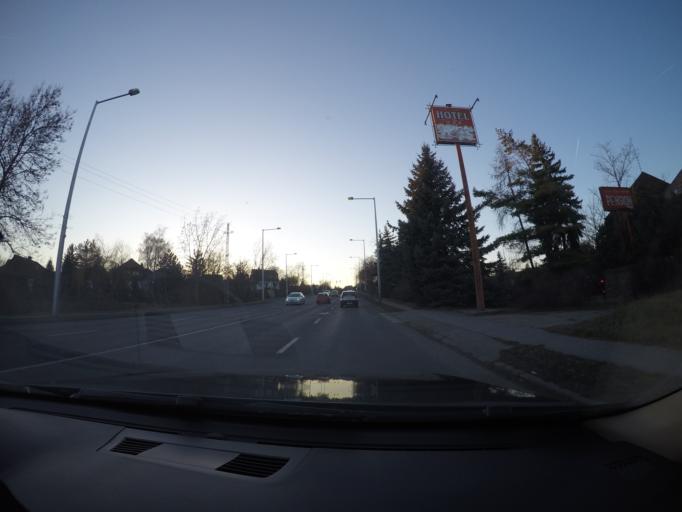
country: HU
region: Pest
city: Szentendre
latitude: 47.6767
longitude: 19.0758
